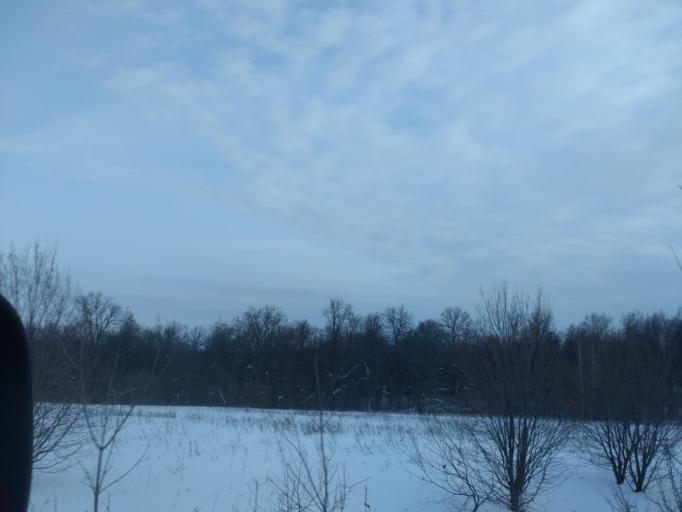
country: RU
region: Bashkortostan
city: Kudeyevskiy
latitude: 54.7258
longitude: 56.6107
